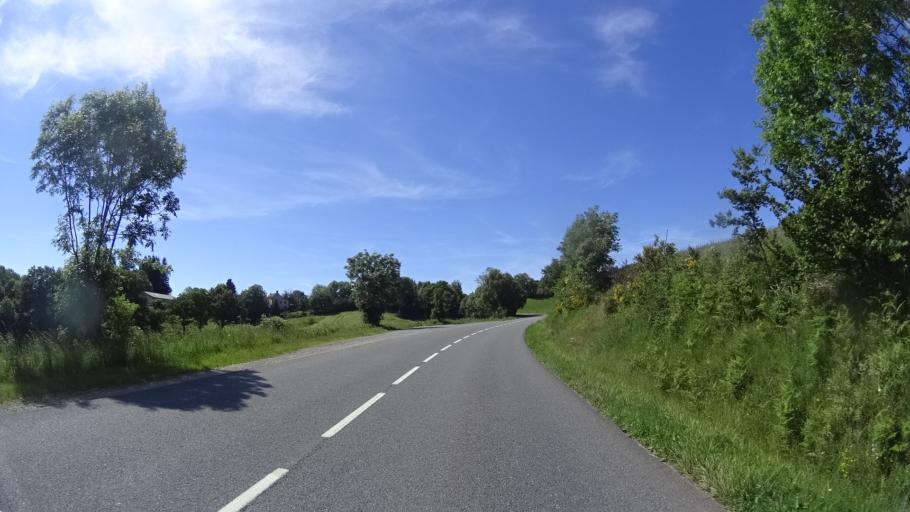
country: FR
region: Midi-Pyrenees
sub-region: Departement de l'Aveyron
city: Pont-de-Salars
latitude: 44.3303
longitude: 2.7736
